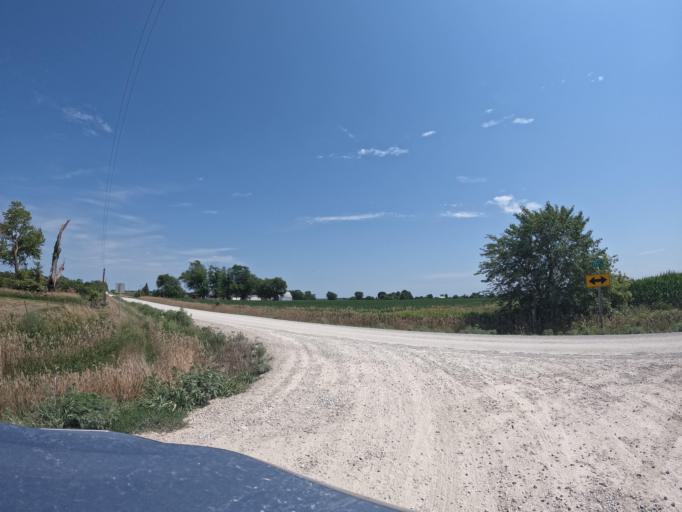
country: US
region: Iowa
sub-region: Henry County
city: Mount Pleasant
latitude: 40.9086
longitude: -91.6365
